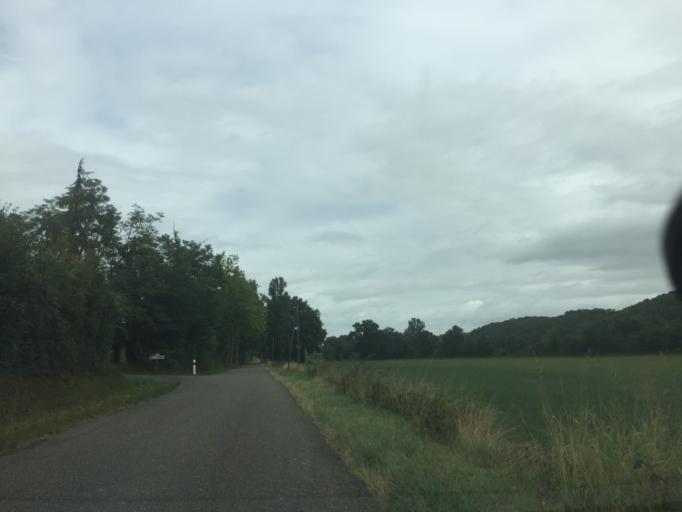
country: FR
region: Midi-Pyrenees
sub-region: Departement du Gers
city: Mielan
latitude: 43.5106
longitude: 0.3207
